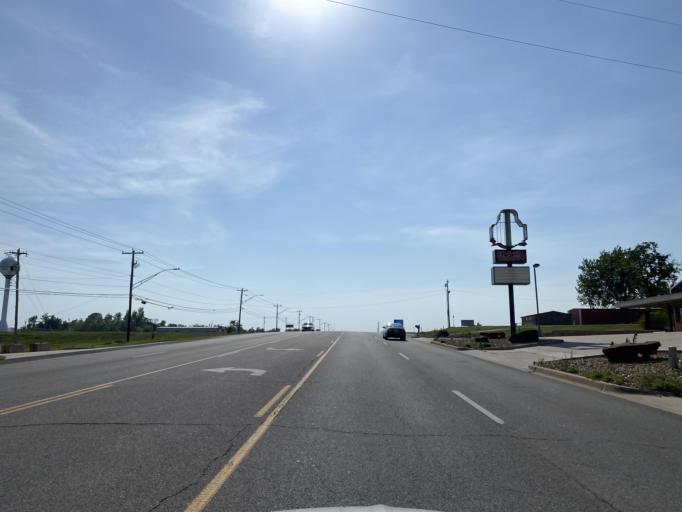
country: US
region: Oklahoma
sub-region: Oklahoma County
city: Nicoma Park
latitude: 35.4931
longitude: -97.3394
